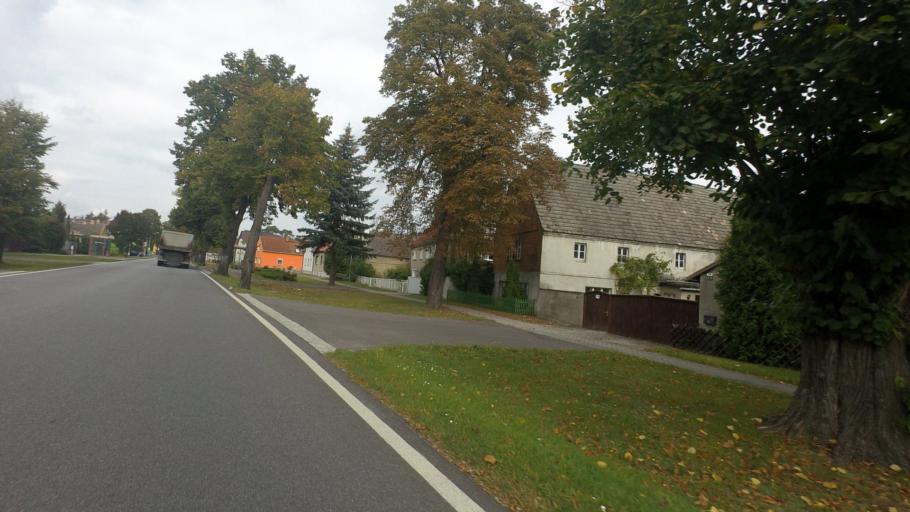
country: DE
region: Brandenburg
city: Bad Liebenwerda
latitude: 51.5484
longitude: 13.3839
